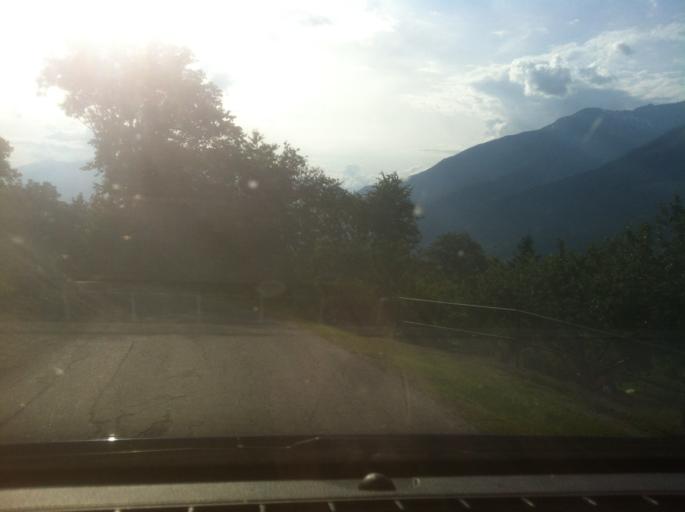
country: IT
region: Aosta Valley
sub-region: Valle d'Aosta
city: Saint Marcel
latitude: 45.7233
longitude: 7.4563
